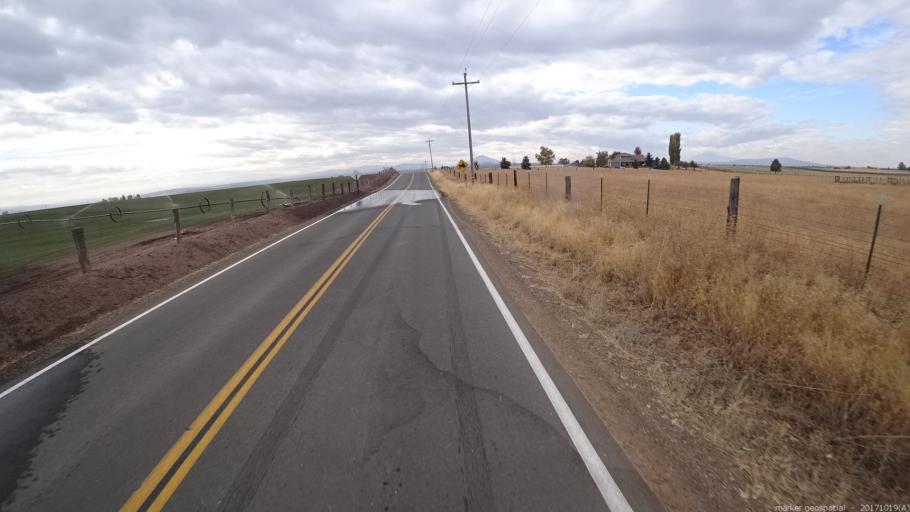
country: US
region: California
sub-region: Shasta County
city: Burney
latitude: 41.0357
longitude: -121.3459
